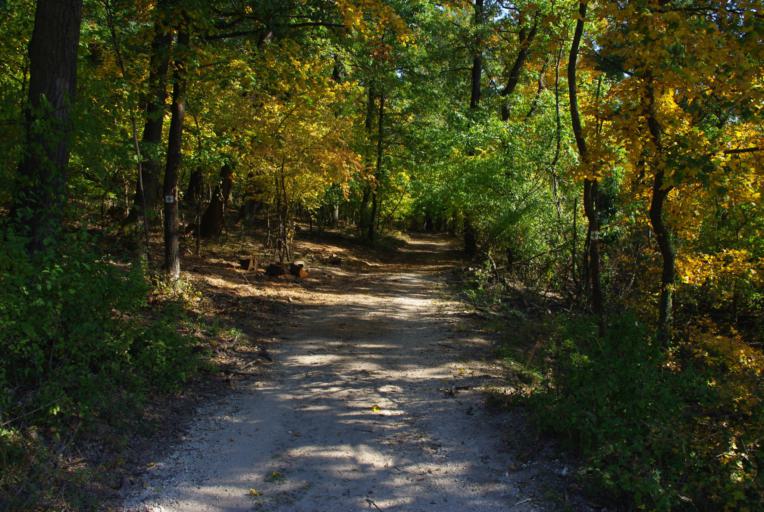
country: HU
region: Pest
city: Budakeszi
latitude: 47.5340
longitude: 18.9200
